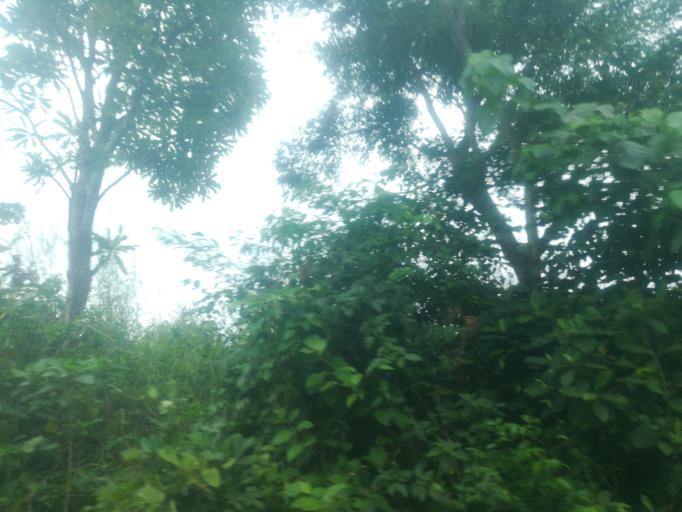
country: NG
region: Ogun
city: Ayetoro
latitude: 7.1047
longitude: 3.1446
